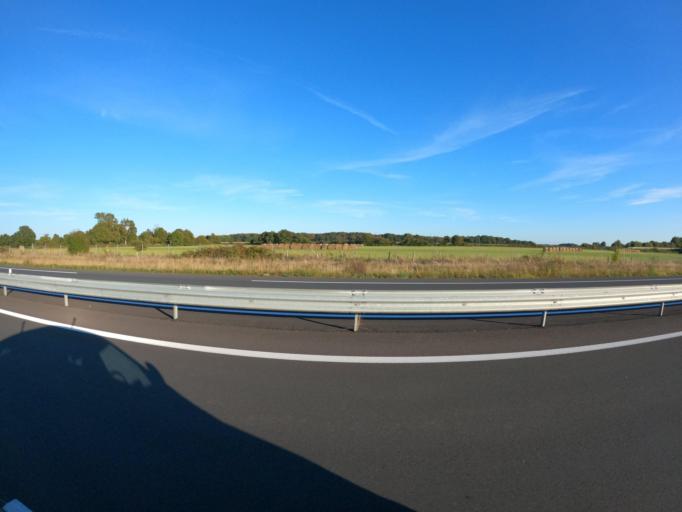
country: FR
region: Pays de la Loire
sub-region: Departement de la Vendee
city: Saint-Fulgent
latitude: 46.8609
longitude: -1.1405
